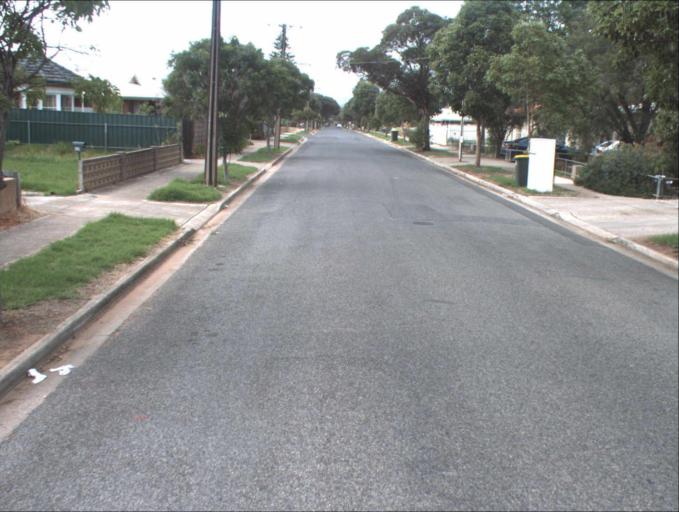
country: AU
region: South Australia
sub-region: Port Adelaide Enfield
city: Klemzig
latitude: -34.8770
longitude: 138.6440
